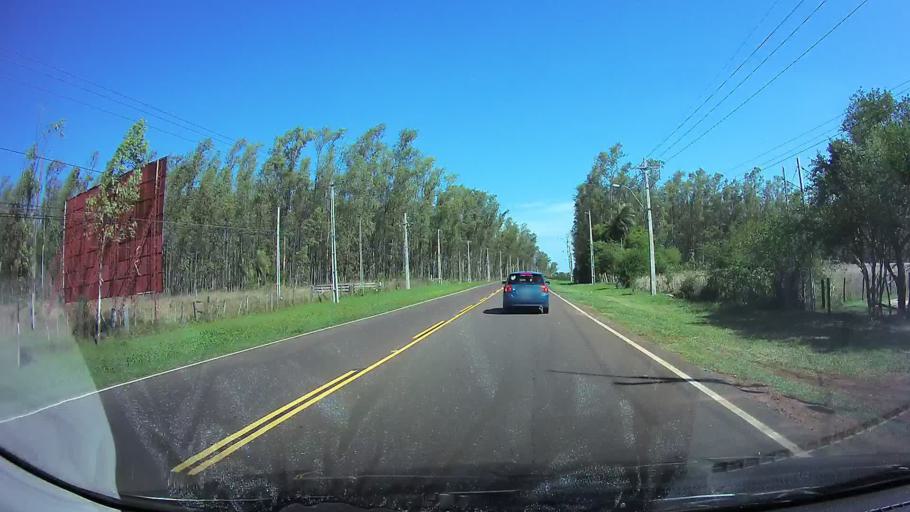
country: PY
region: Central
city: Ypacarai
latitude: -25.3736
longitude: -57.2631
